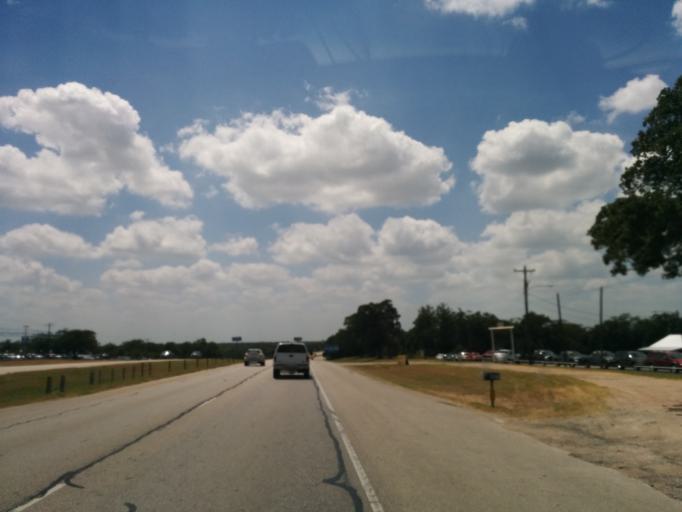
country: US
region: Texas
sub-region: Bastrop County
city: Wyldwood
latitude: 30.1108
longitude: -97.4038
